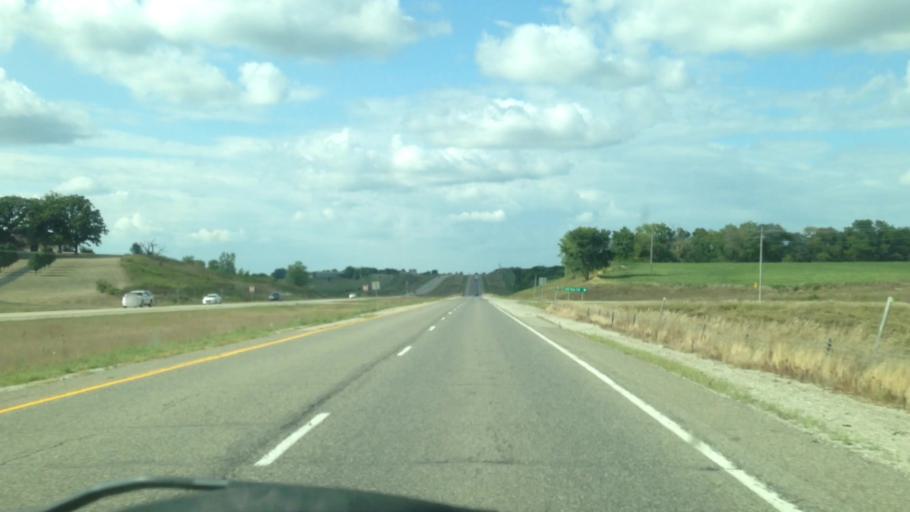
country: US
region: Iowa
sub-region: Henry County
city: Mount Pleasant
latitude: 40.8574
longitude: -91.5647
